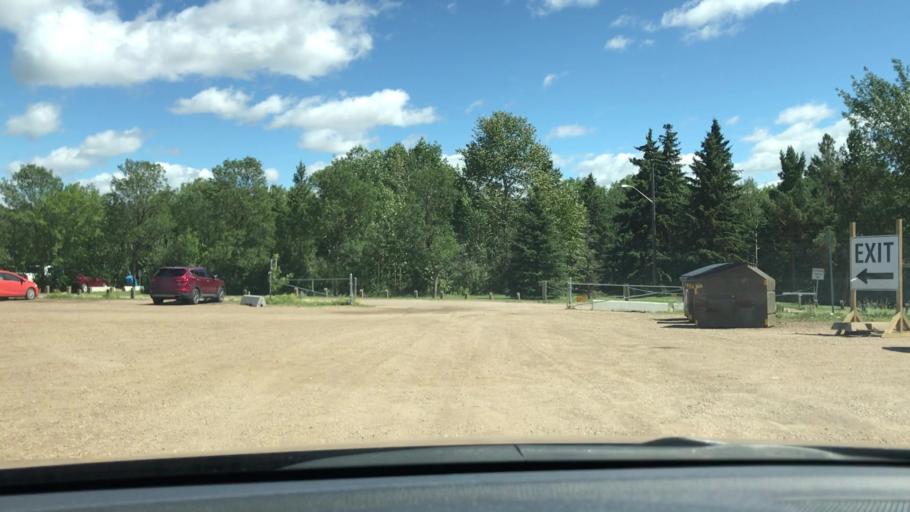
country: CA
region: Alberta
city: Edmonton
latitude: 53.5106
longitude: -113.5516
